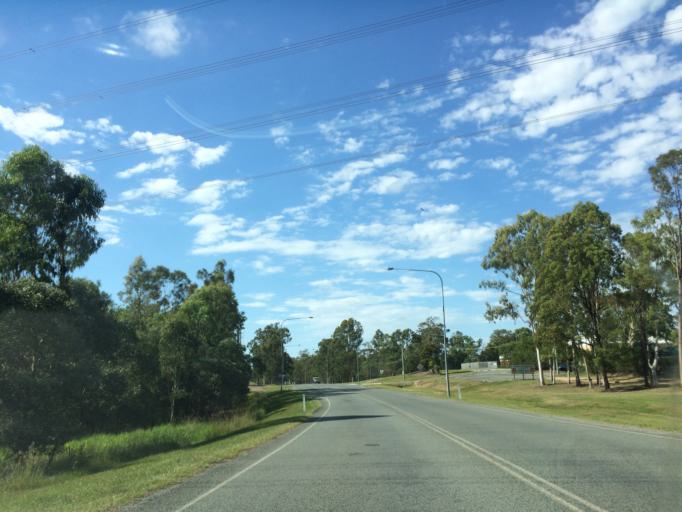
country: AU
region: Queensland
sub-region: Logan
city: Park Ridge South
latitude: -27.7287
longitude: 152.9841
